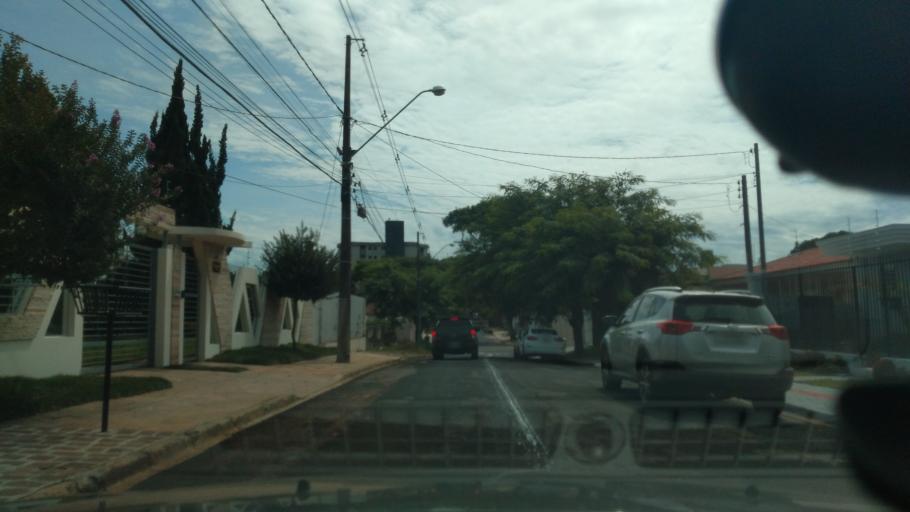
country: BR
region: Parana
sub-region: Guarapuava
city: Guarapuava
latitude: -25.3874
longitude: -51.4672
